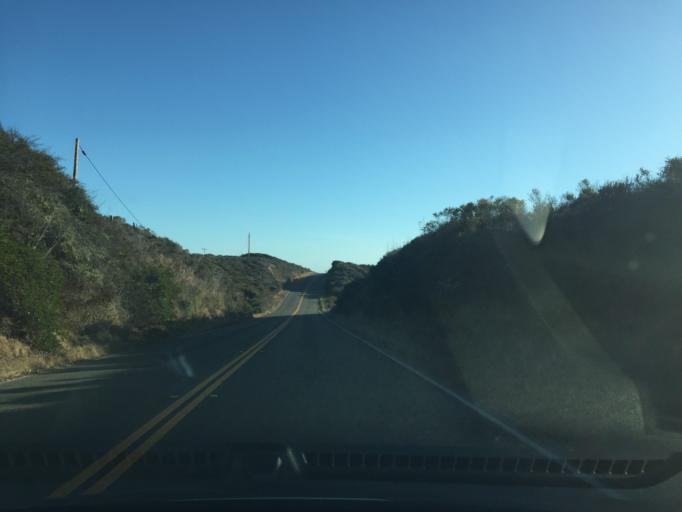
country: US
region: California
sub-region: San Luis Obispo County
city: Cambria
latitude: 35.7503
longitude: -121.3118
